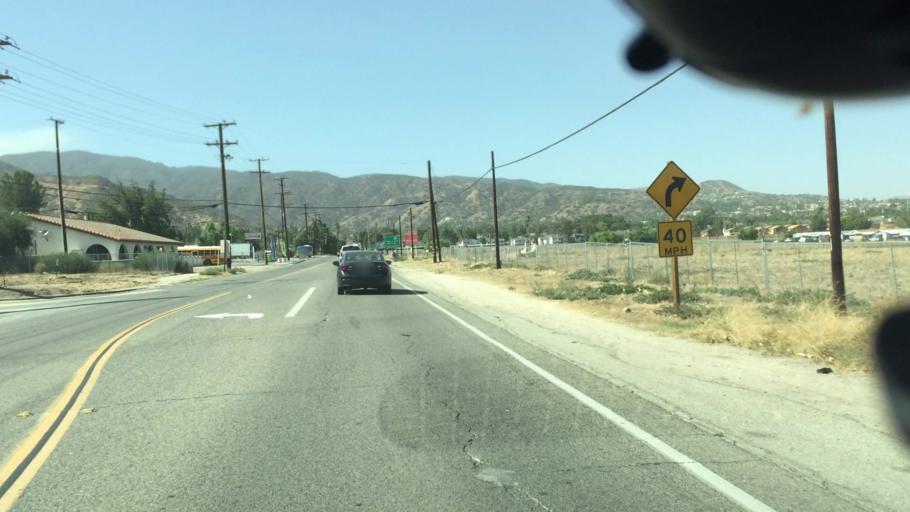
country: US
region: California
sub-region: Riverside County
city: Lakeland Village
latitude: 33.6618
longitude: -117.3814
